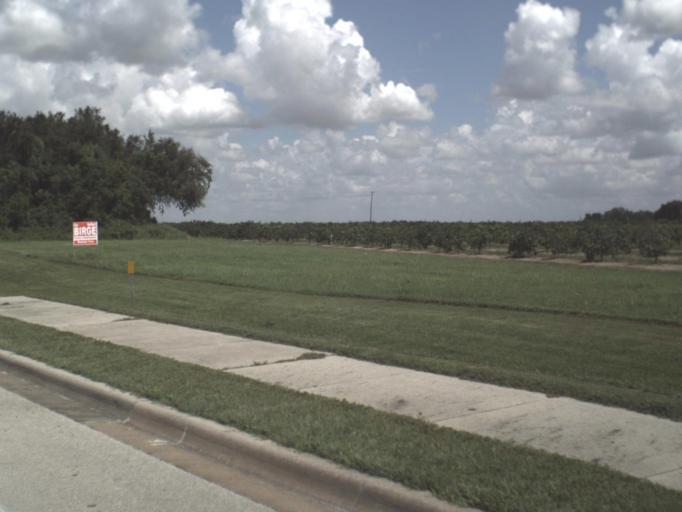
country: US
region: Florida
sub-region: Hardee County
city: Wauchula
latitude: 27.5610
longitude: -81.8138
